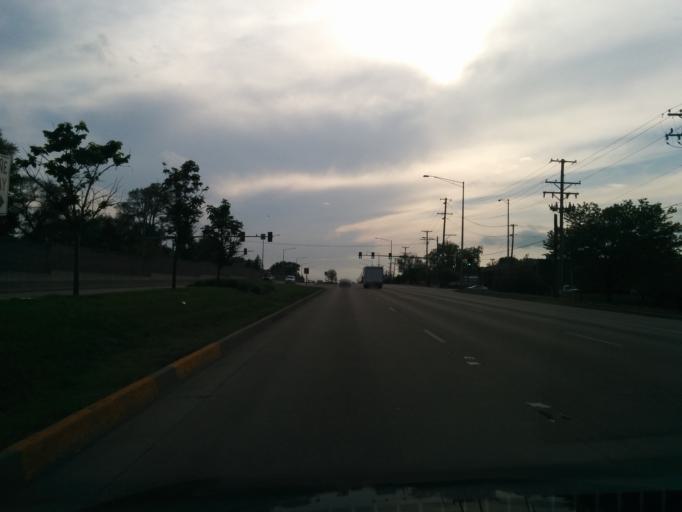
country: US
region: Illinois
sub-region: DuPage County
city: Lombard
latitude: 41.9047
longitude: -88.0233
